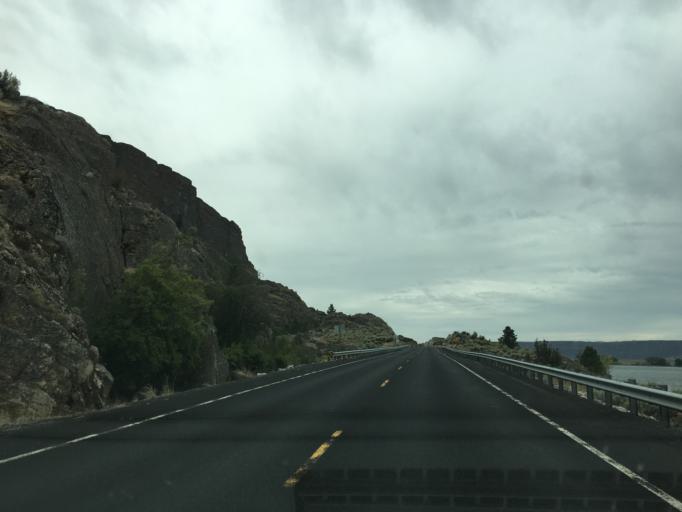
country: US
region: Washington
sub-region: Okanogan County
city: Coulee Dam
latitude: 47.8551
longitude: -119.1071
